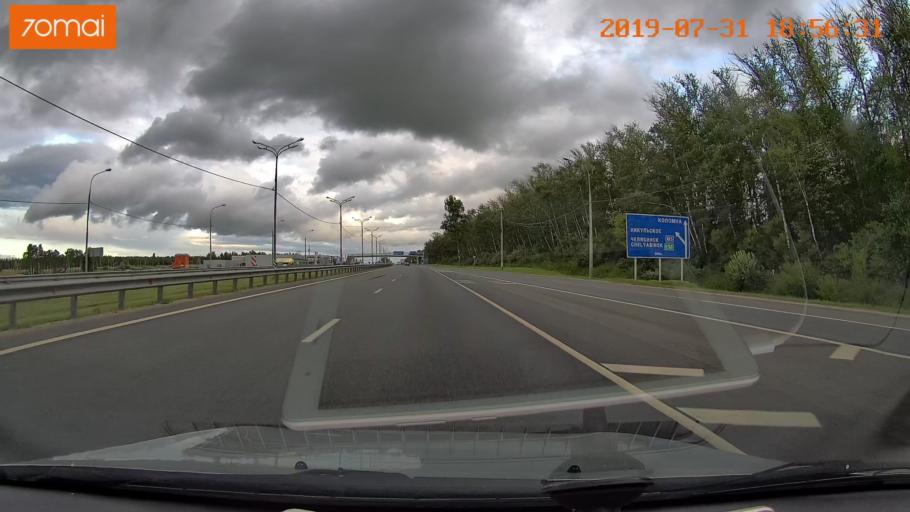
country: RU
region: Moskovskaya
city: Raduzhnyy
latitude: 55.1624
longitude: 38.6790
